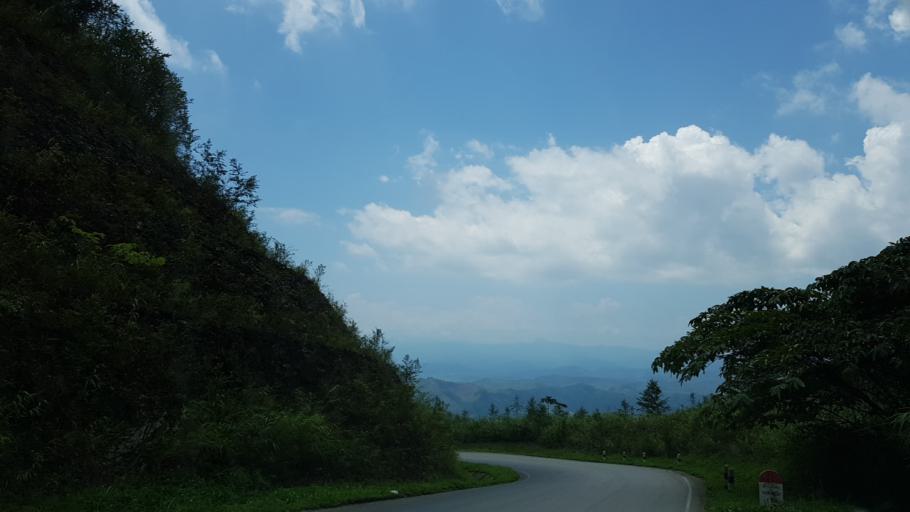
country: LA
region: Vientiane
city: Muang Kasi
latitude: 19.3807
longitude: 102.1551
